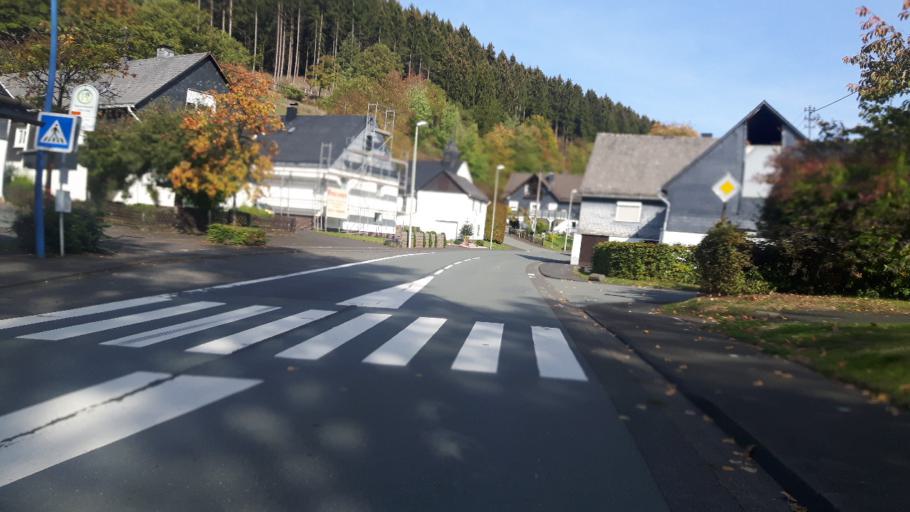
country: DE
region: North Rhine-Westphalia
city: Netphen
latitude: 50.8936
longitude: 8.1899
